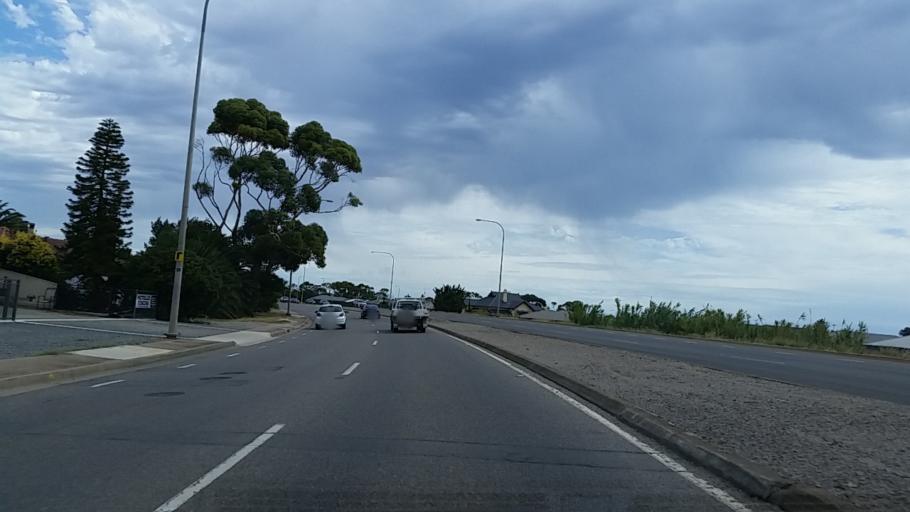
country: AU
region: South Australia
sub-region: Onkaparinga
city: Noarlunga
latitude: -35.1877
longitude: 138.4905
